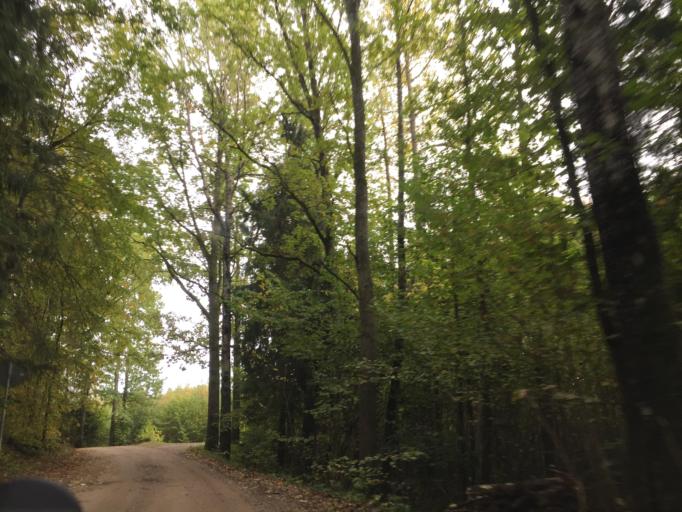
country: LV
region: Auces Novads
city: Auce
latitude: 56.5462
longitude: 23.0187
